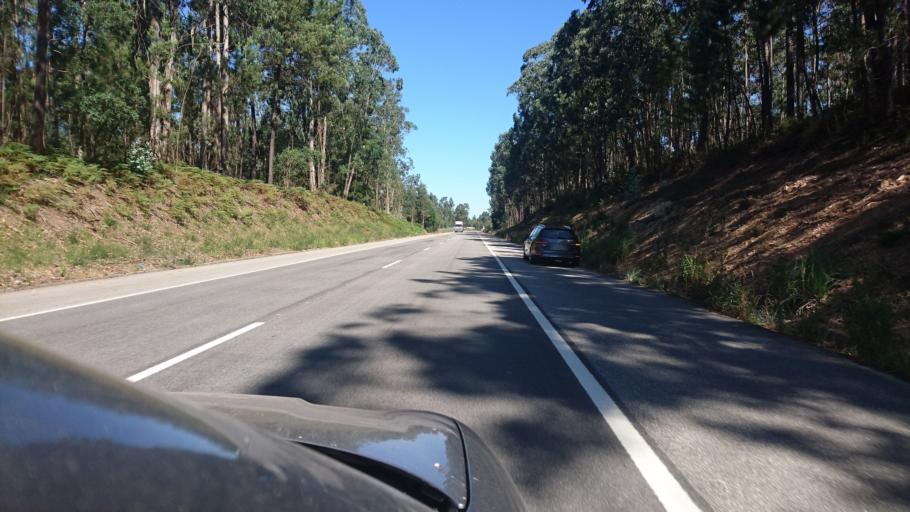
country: PT
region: Aveiro
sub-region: Santa Maria da Feira
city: Rio Meao
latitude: 40.9436
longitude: -8.5849
